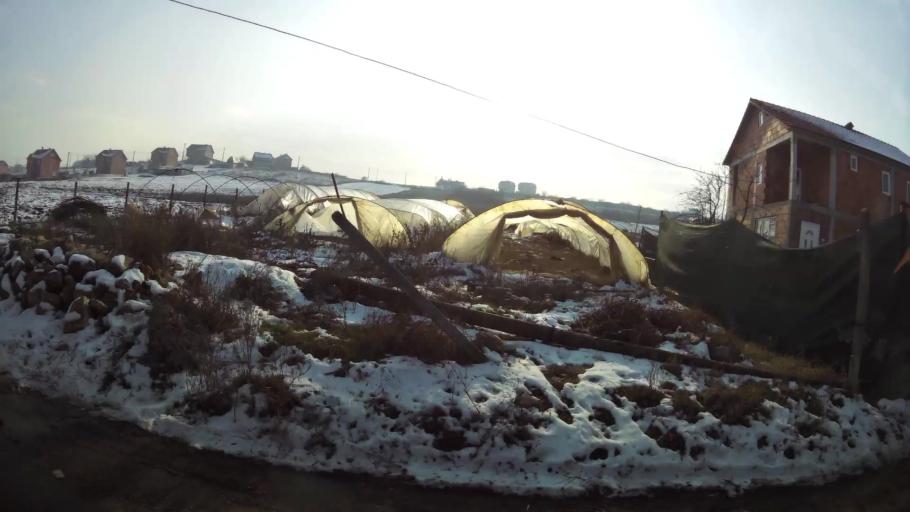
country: MK
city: Creshevo
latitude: 42.0204
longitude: 21.4998
